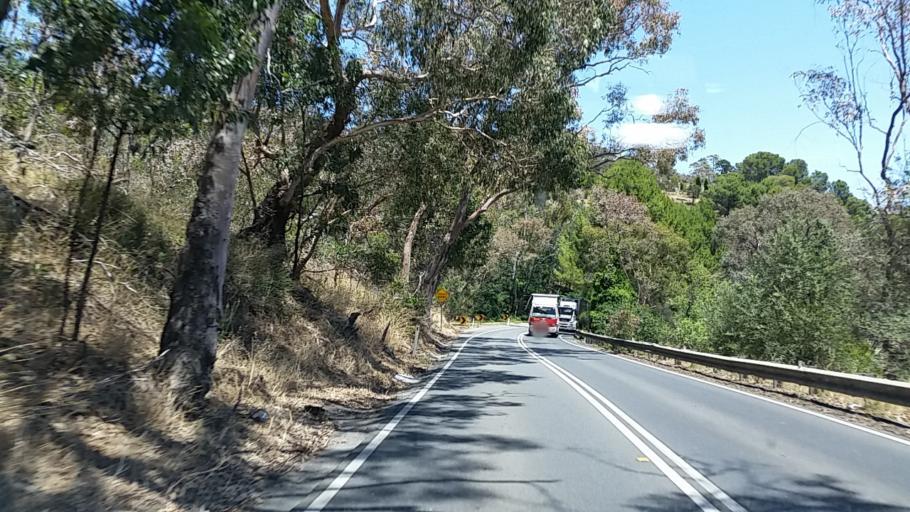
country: AU
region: South Australia
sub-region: Tea Tree Gully
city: Golden Grove
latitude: -34.8255
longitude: 138.7493
